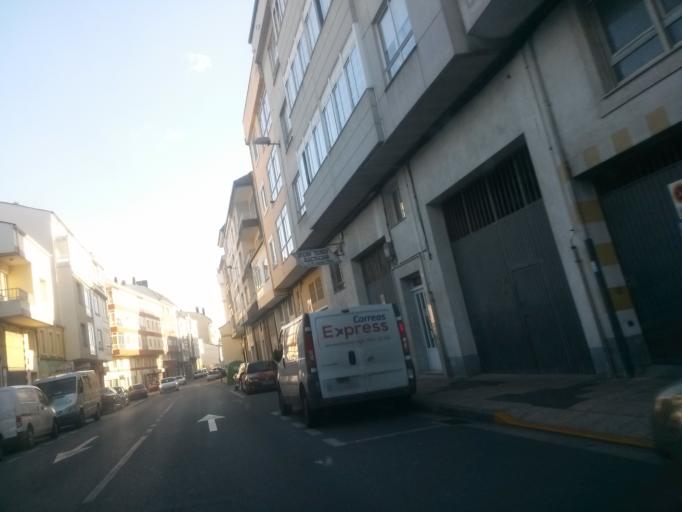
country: ES
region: Galicia
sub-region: Provincia de Lugo
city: Lugo
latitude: 43.0281
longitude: -7.5718
